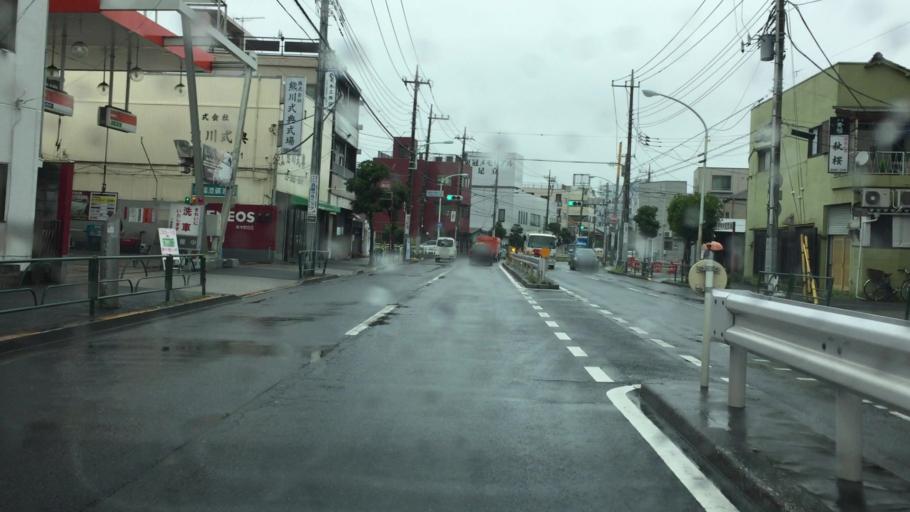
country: JP
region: Saitama
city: Soka
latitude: 35.7633
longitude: 139.7873
